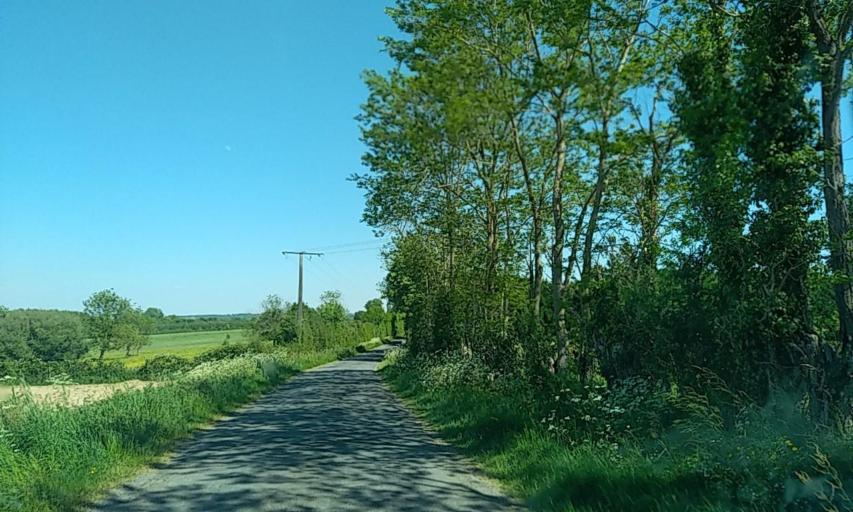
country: FR
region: Poitou-Charentes
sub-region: Departement des Deux-Sevres
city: Boisme
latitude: 46.7687
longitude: -0.4595
